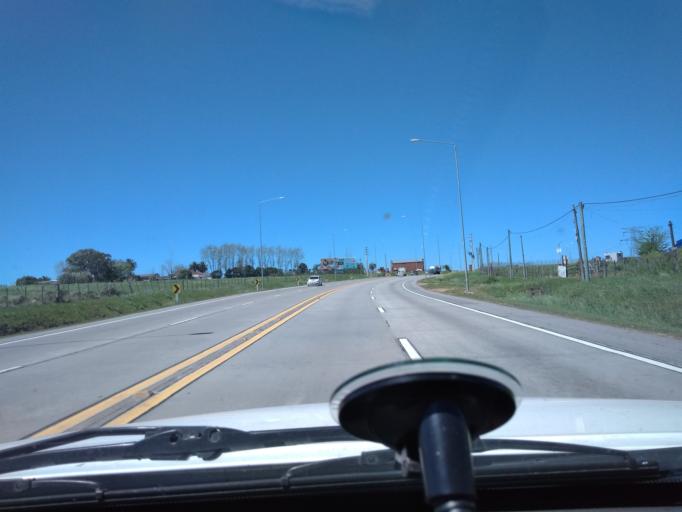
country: UY
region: Canelones
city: La Paz
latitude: -34.7932
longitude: -56.1720
